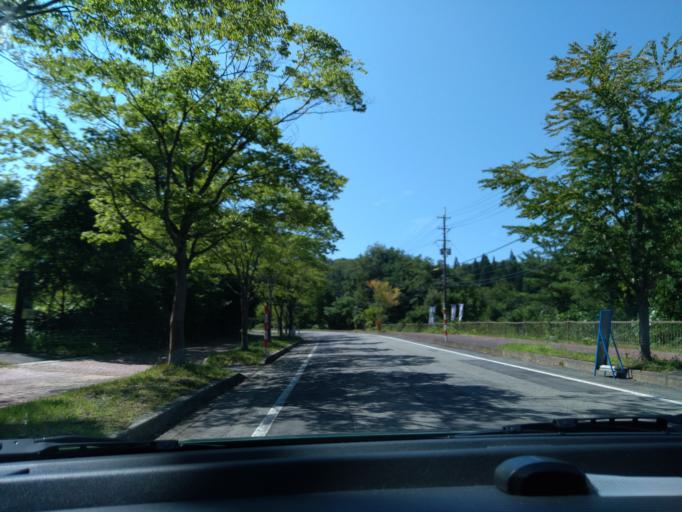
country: JP
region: Akita
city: Kakunodatemachi
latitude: 39.7352
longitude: 140.7042
